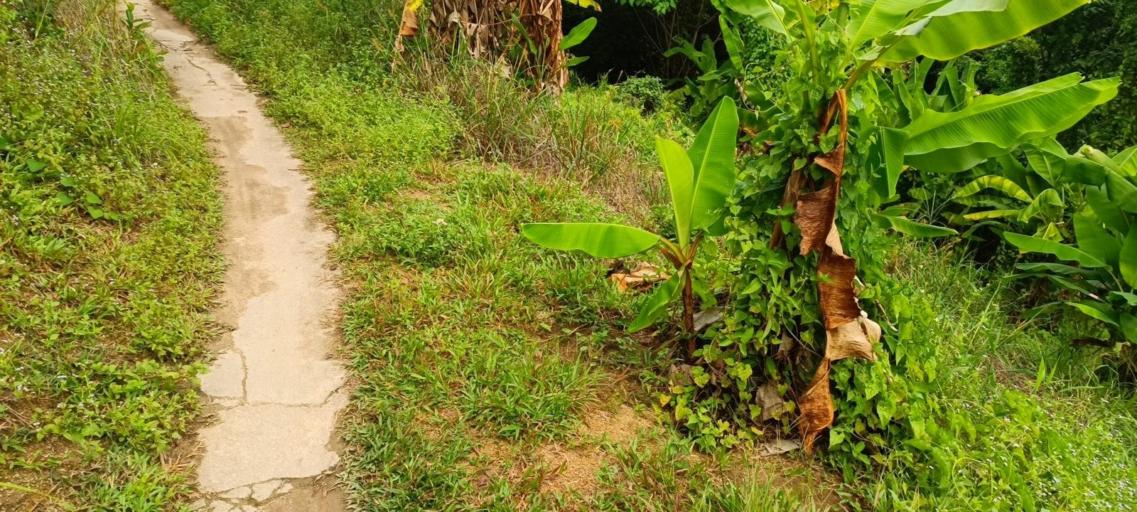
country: MY
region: Penang
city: Kampung Sungai Ara
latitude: 5.2932
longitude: 100.1863
